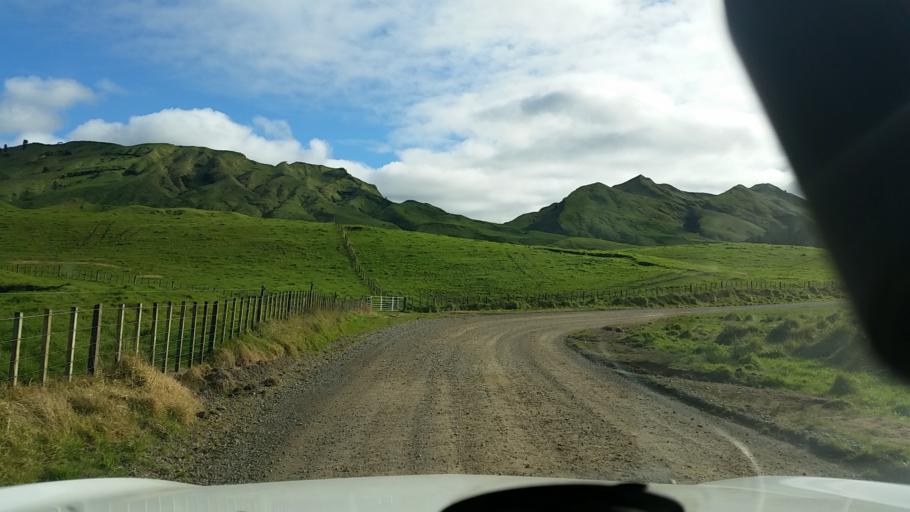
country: NZ
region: Hawke's Bay
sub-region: Napier City
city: Napier
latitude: -39.1268
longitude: 176.8950
